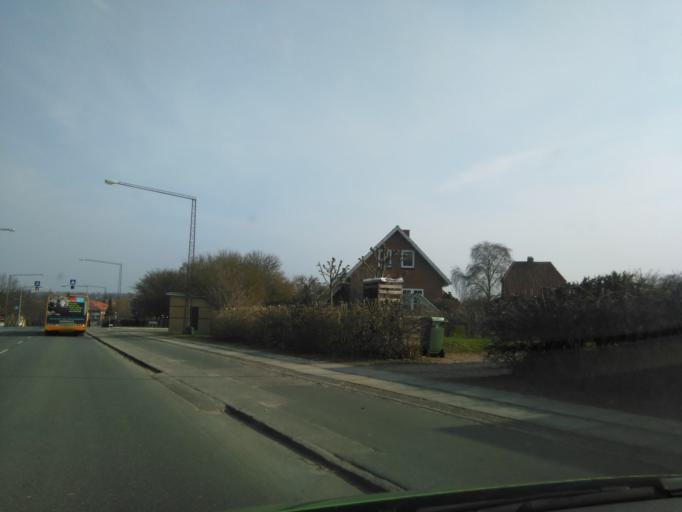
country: DK
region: Central Jutland
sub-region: Arhus Kommune
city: Arhus
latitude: 56.1934
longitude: 10.2332
